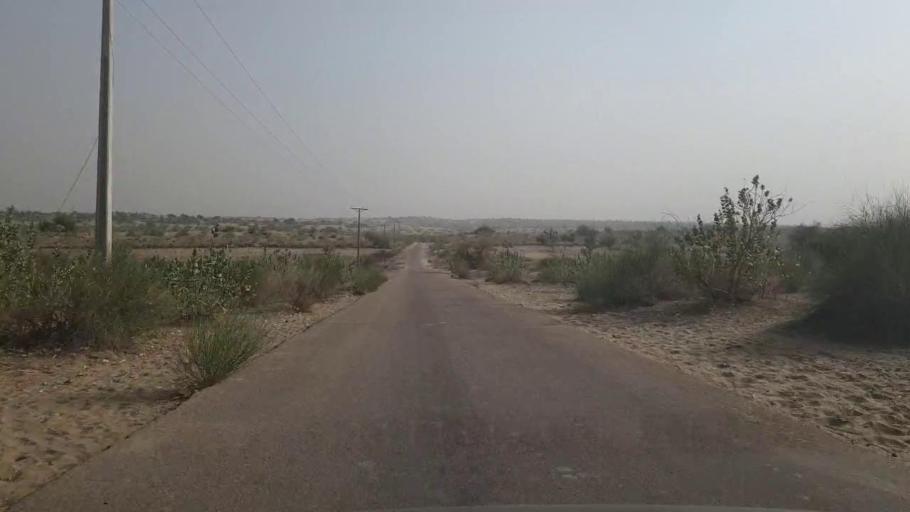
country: PK
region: Sindh
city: Chor
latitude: 25.5453
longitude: 69.9595
